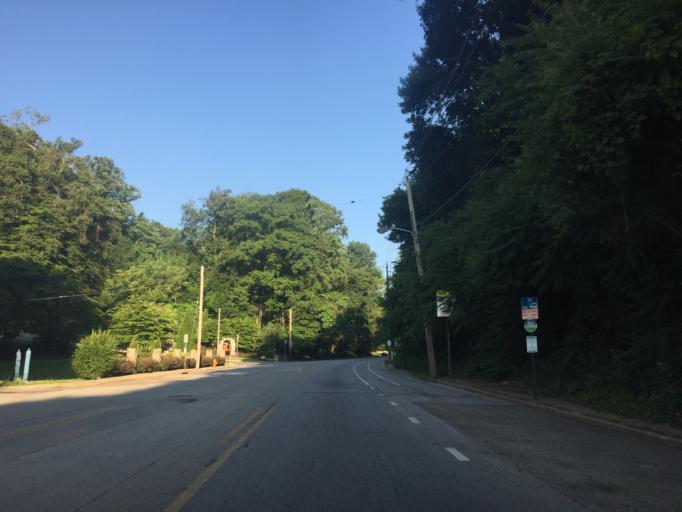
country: US
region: Maryland
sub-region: Baltimore County
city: Charlestown
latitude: 39.2810
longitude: -76.7018
